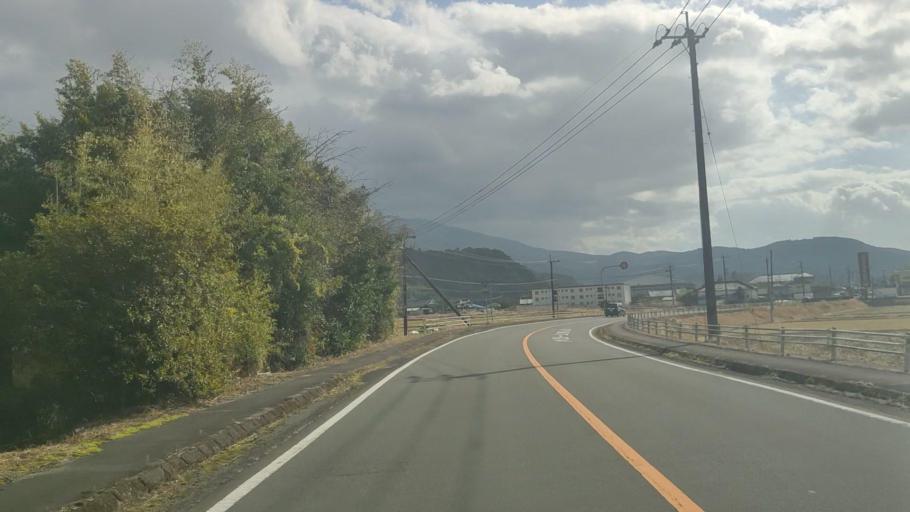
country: JP
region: Kagoshima
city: Okuchi-shinohara
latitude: 32.0209
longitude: 130.7435
